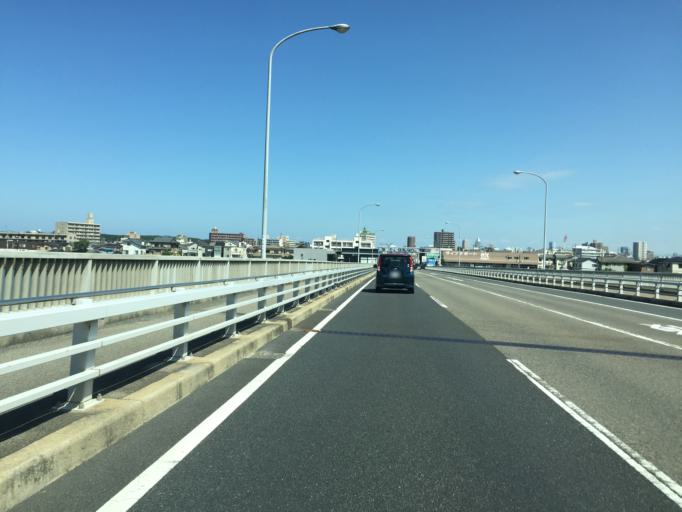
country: JP
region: Niigata
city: Niigata-shi
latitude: 37.9014
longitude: 139.0070
